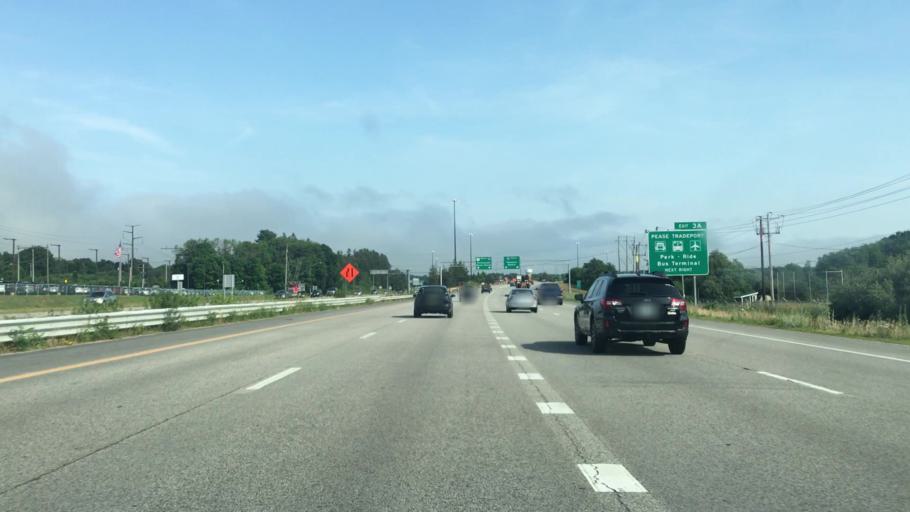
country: US
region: Maine
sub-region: York County
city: South Eliot
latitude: 43.0838
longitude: -70.7945
